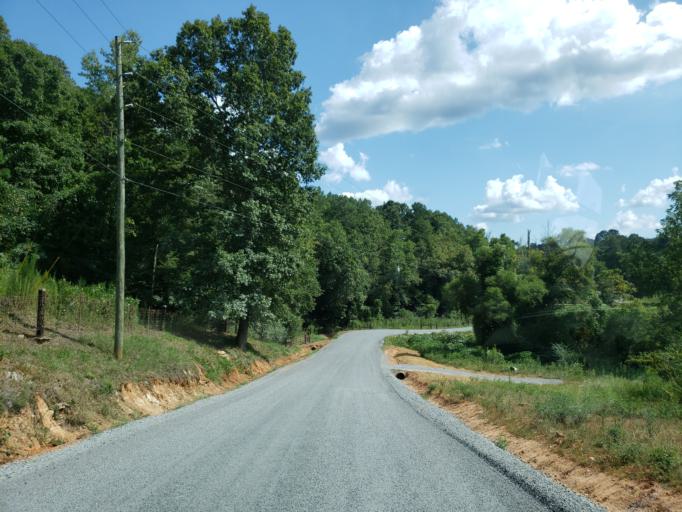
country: US
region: Georgia
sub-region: Pickens County
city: Jasper
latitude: 34.4217
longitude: -84.4571
